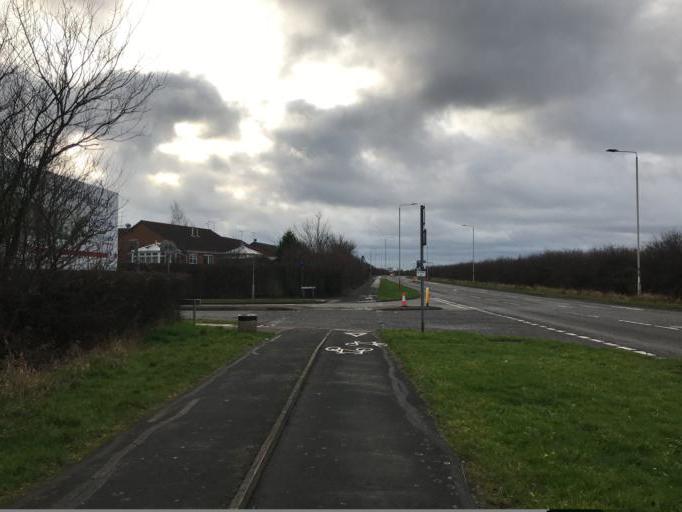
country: GB
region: England
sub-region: Leicestershire
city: Hinckley
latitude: 52.5472
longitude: -1.3990
